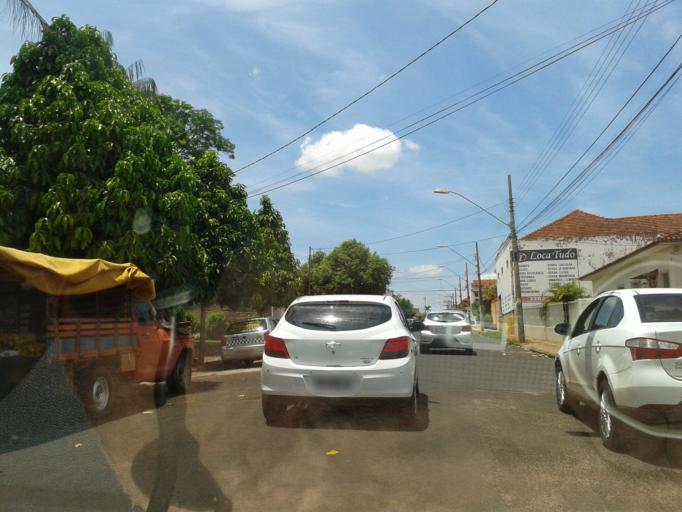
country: BR
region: Minas Gerais
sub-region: Ituiutaba
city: Ituiutaba
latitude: -18.9795
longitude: -49.4600
